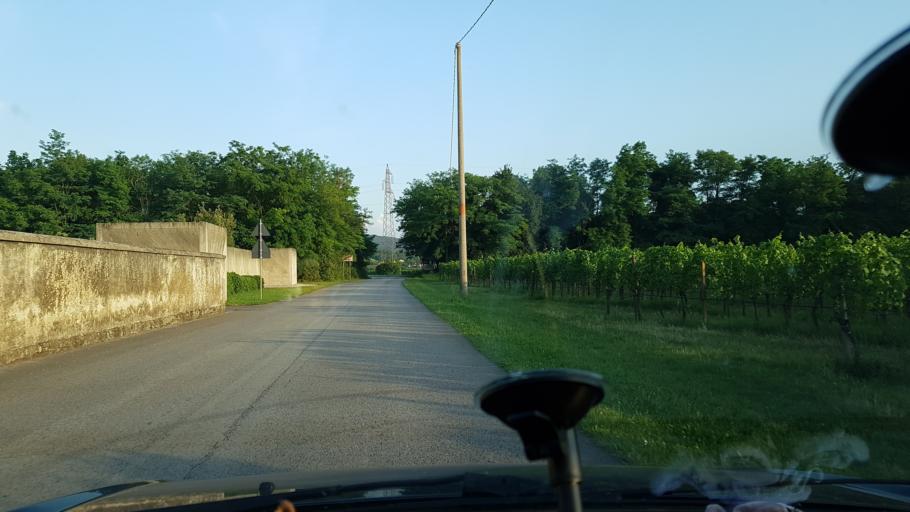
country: IT
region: Friuli Venezia Giulia
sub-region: Provincia di Gorizia
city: San Lorenzo Isontino
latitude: 45.9225
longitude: 13.5295
